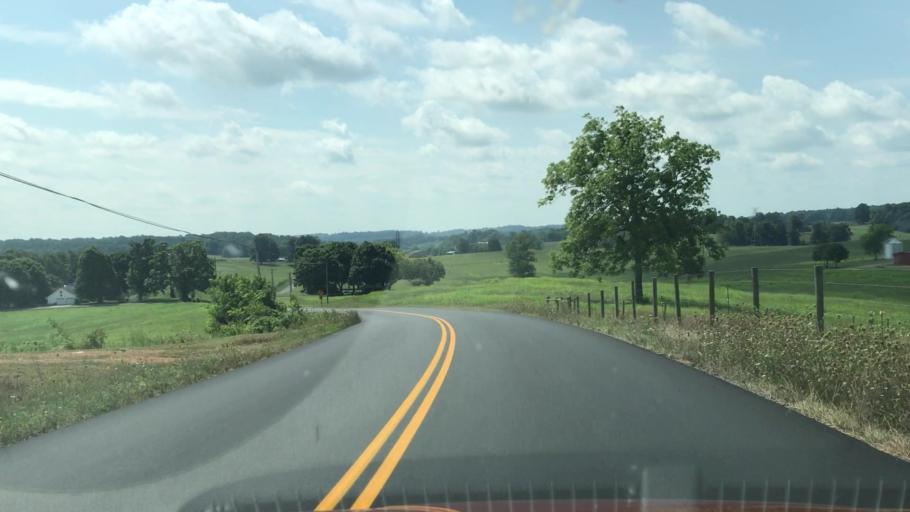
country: US
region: Kentucky
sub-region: Monroe County
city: Tompkinsville
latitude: 36.7994
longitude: -85.8200
